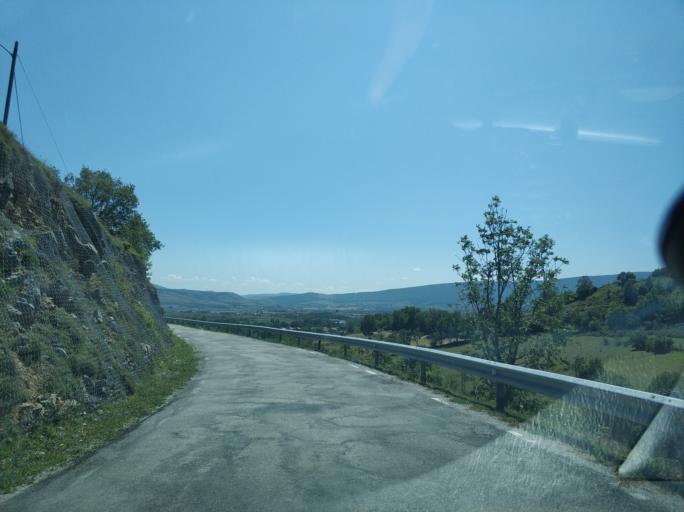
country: ES
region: Cantabria
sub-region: Provincia de Cantabria
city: Reinosa
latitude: 43.0255
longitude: -4.1691
